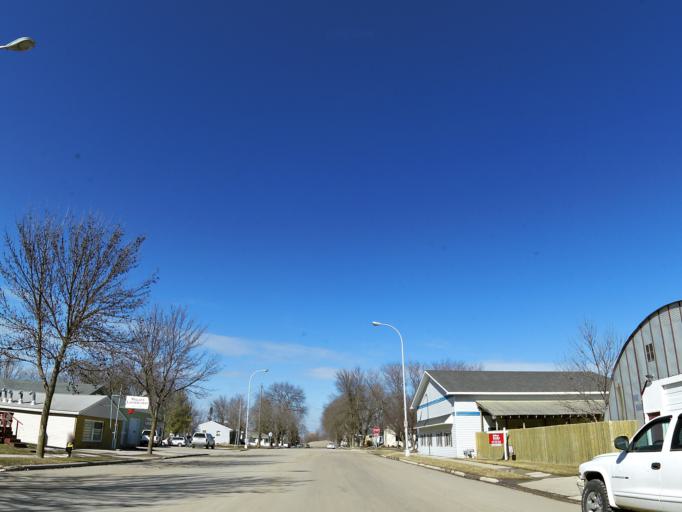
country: US
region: Minnesota
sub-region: Waseca County
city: New Richland
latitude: 43.8964
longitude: -93.4939
